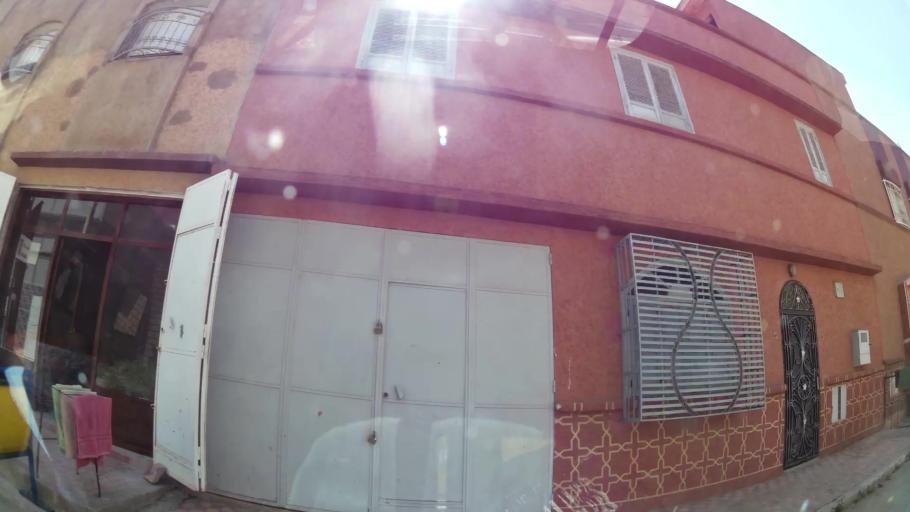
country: MA
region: Rabat-Sale-Zemmour-Zaer
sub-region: Khemisset
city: Khemisset
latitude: 33.8119
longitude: -6.0745
